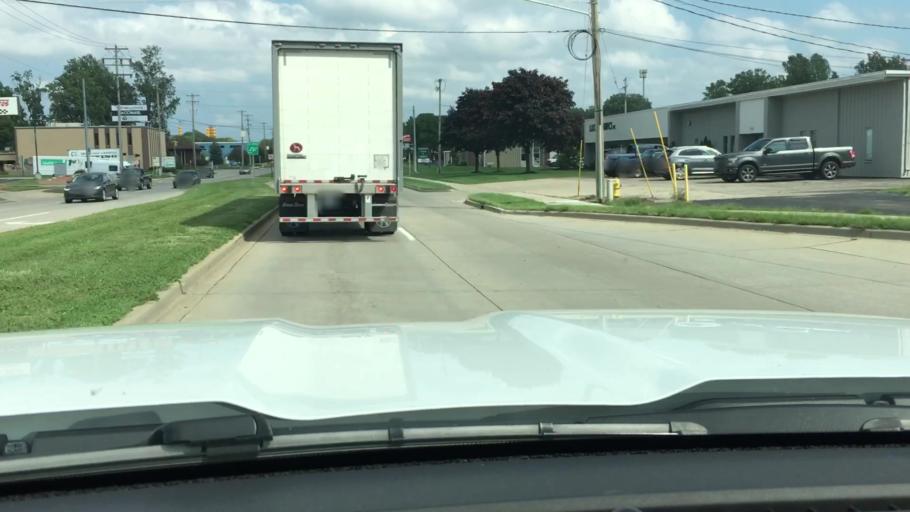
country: US
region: Michigan
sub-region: Kent County
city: Kentwood
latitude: 42.8838
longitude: -85.6532
